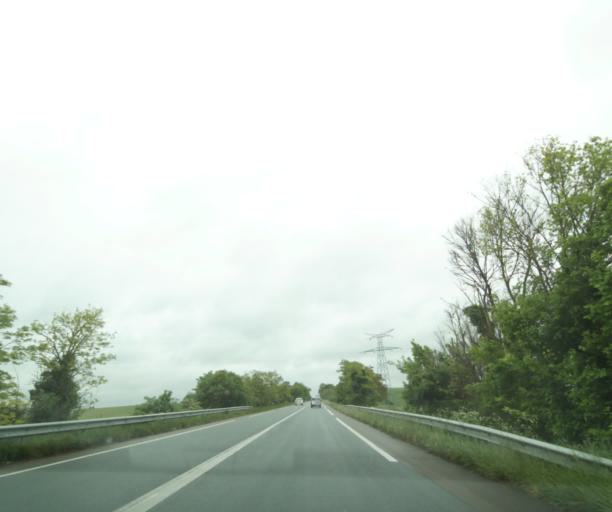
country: FR
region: Poitou-Charentes
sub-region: Departement de la Charente-Maritime
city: Les Gonds
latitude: 45.6821
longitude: -0.6091
